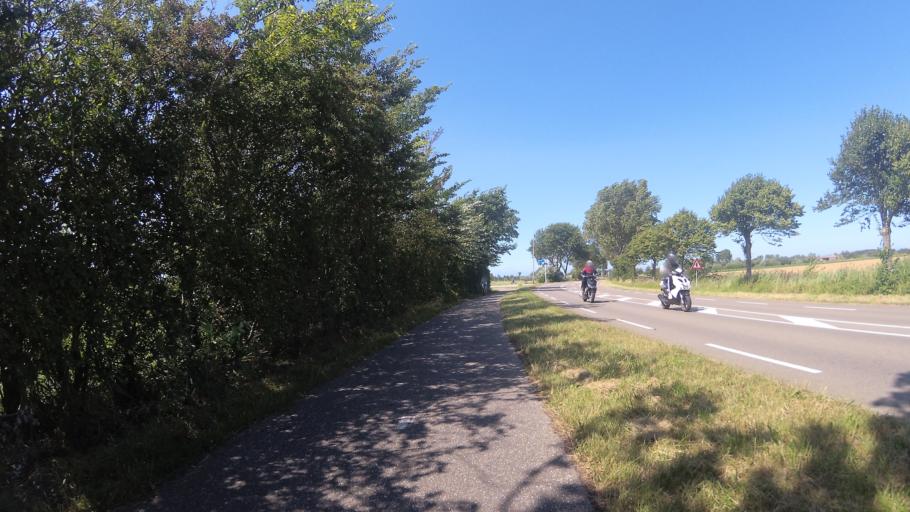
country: NL
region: Zeeland
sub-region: Gemeente Vlissingen
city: Vlissingen
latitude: 51.4826
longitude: 3.5409
